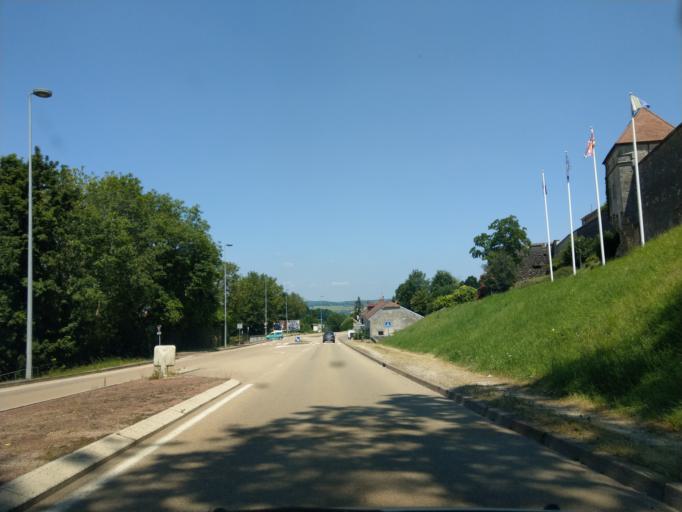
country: FR
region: Champagne-Ardenne
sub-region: Departement de la Haute-Marne
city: Langres
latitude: 47.8655
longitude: 5.3300
